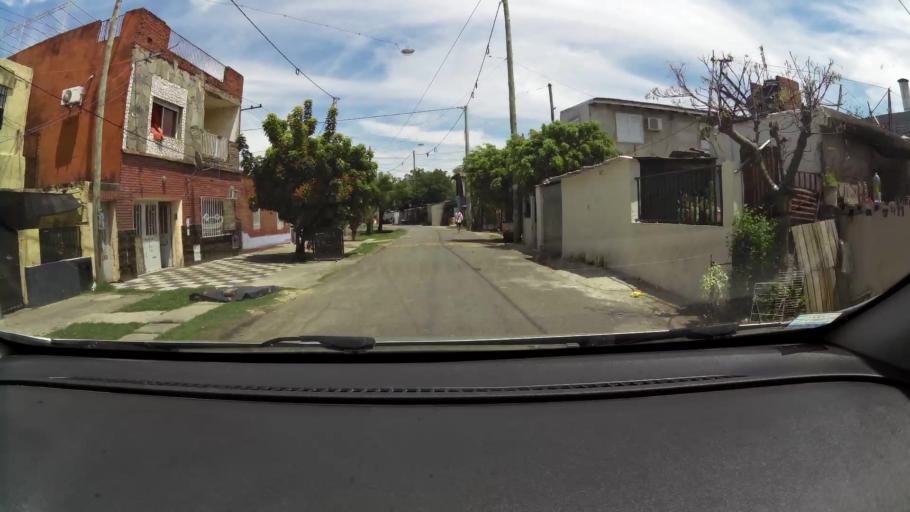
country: AR
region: Santa Fe
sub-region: Departamento de Rosario
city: Rosario
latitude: -32.9842
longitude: -60.6257
